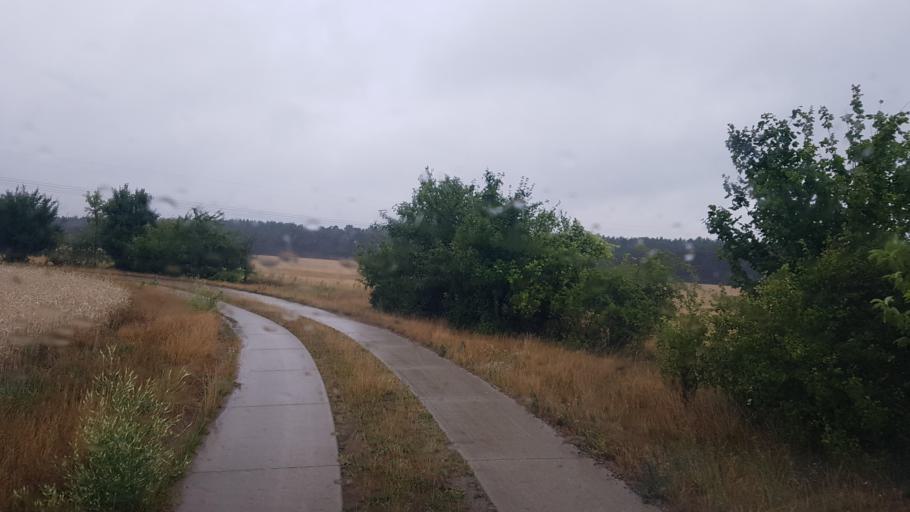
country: DE
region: Brandenburg
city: Trebbin
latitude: 52.1886
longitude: 13.2589
